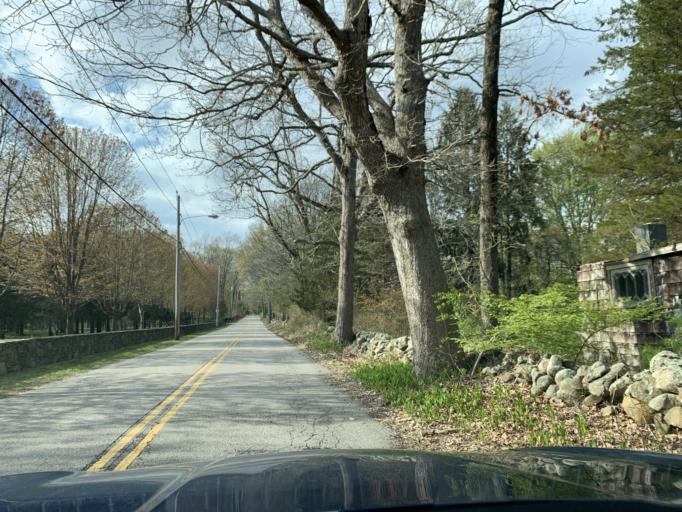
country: US
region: Rhode Island
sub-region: Washington County
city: Exeter
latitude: 41.5943
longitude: -71.5185
